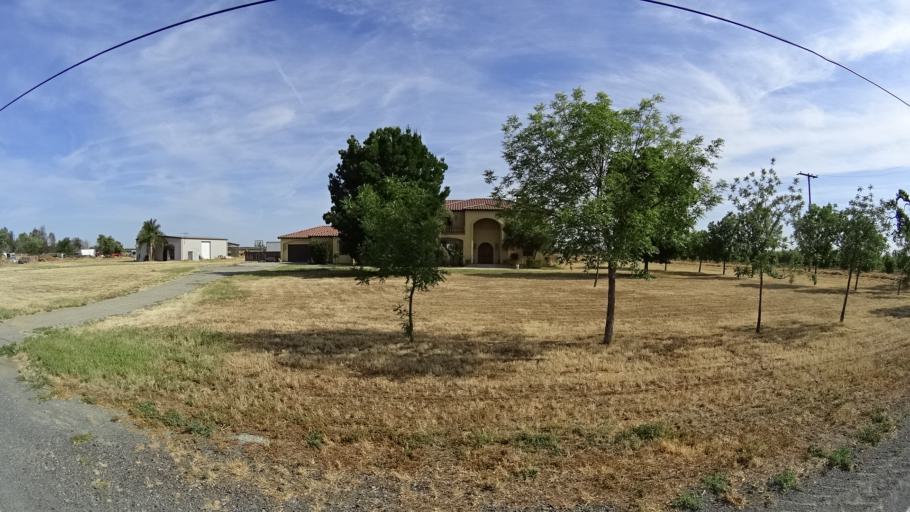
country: US
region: California
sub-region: Kings County
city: Home Garden
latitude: 36.3427
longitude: -119.5699
